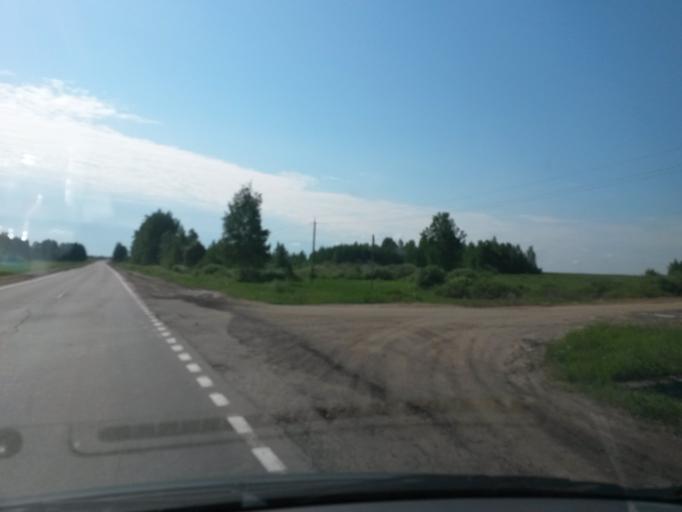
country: RU
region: Jaroslavl
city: Gavrilov-Yam
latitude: 57.3410
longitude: 39.8005
